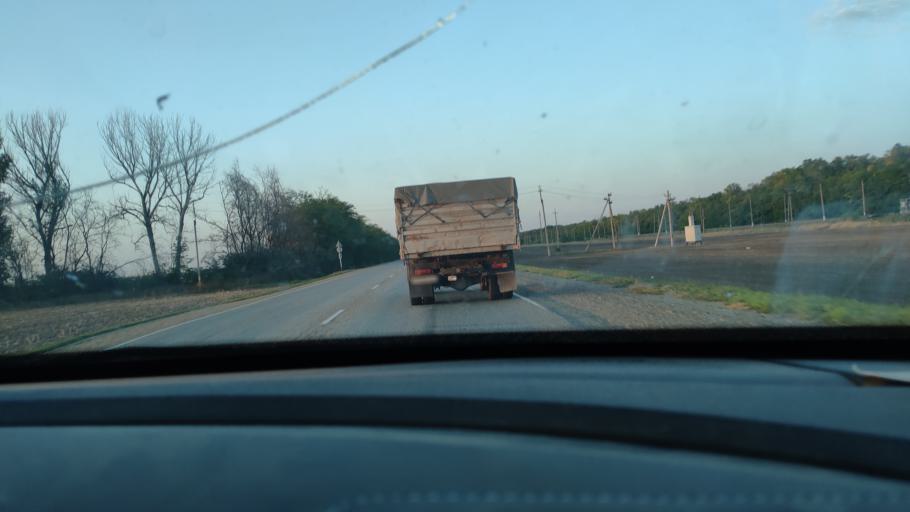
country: RU
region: Krasnodarskiy
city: Starominskaya
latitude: 46.4772
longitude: 39.0489
